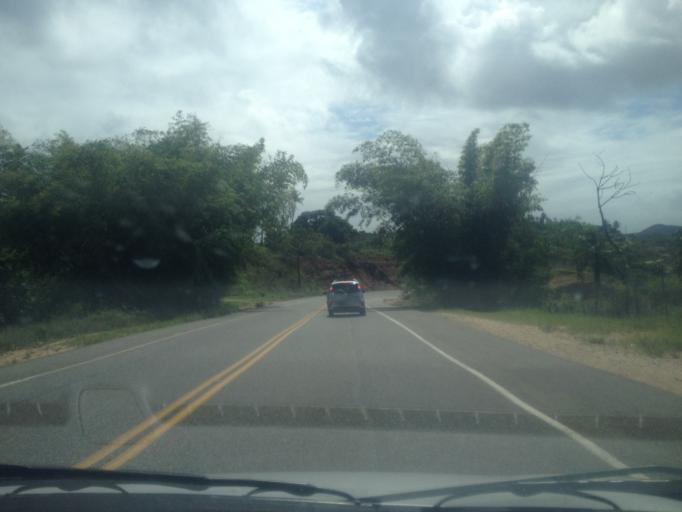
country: BR
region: Bahia
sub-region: Conde
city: Conde
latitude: -11.7140
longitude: -37.5729
